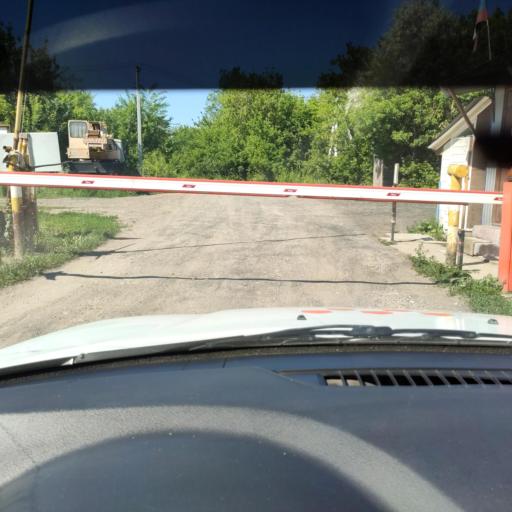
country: RU
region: Samara
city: Tol'yatti
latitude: 53.5674
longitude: 49.3712
